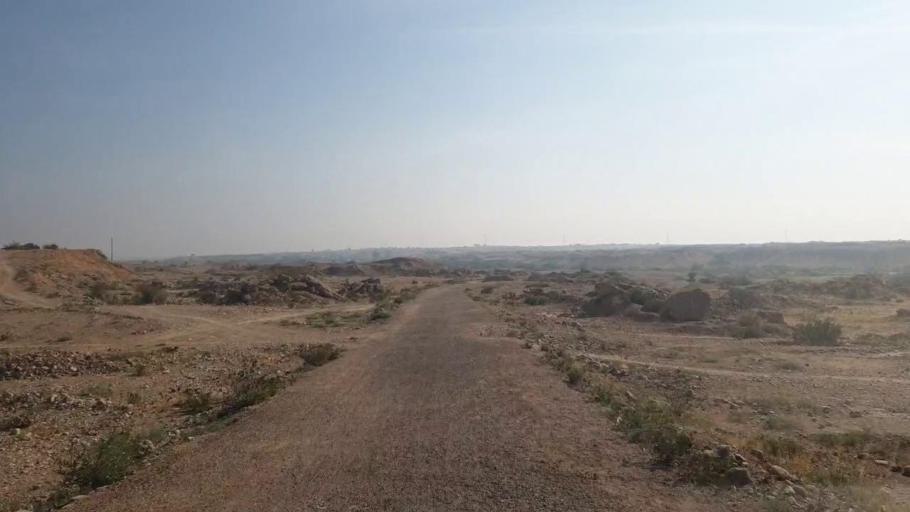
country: PK
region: Sindh
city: Matiari
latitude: 25.6232
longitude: 68.3169
